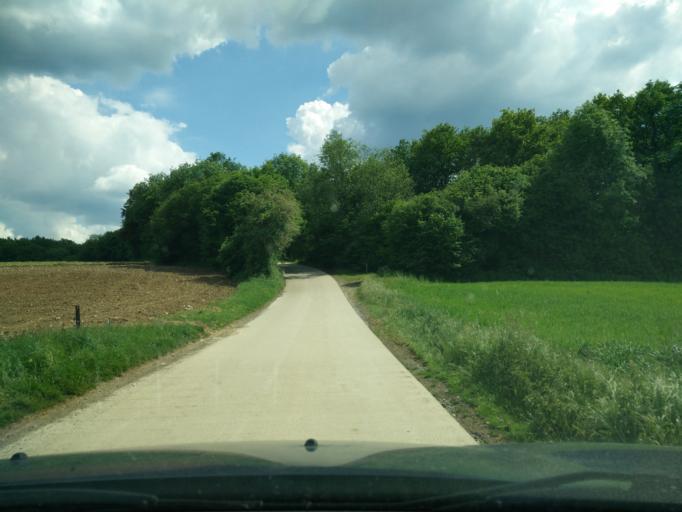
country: BE
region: Wallonia
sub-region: Province de Namur
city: Couvin
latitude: 50.0903
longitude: 4.6064
